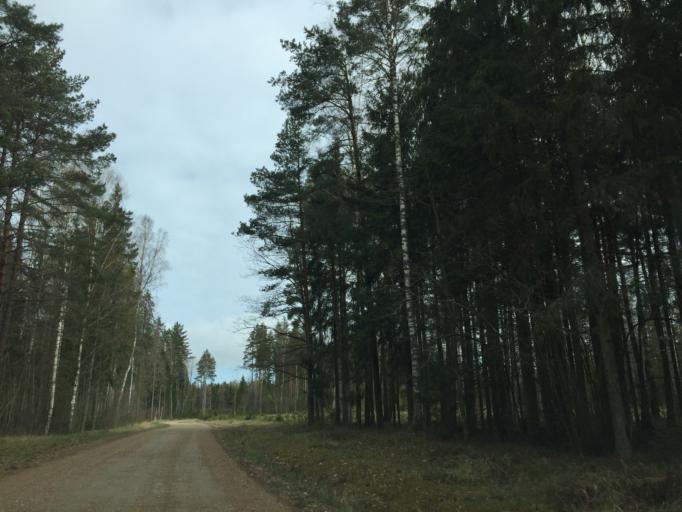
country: LV
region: Saulkrastu
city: Saulkrasti
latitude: 57.5101
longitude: 24.4136
